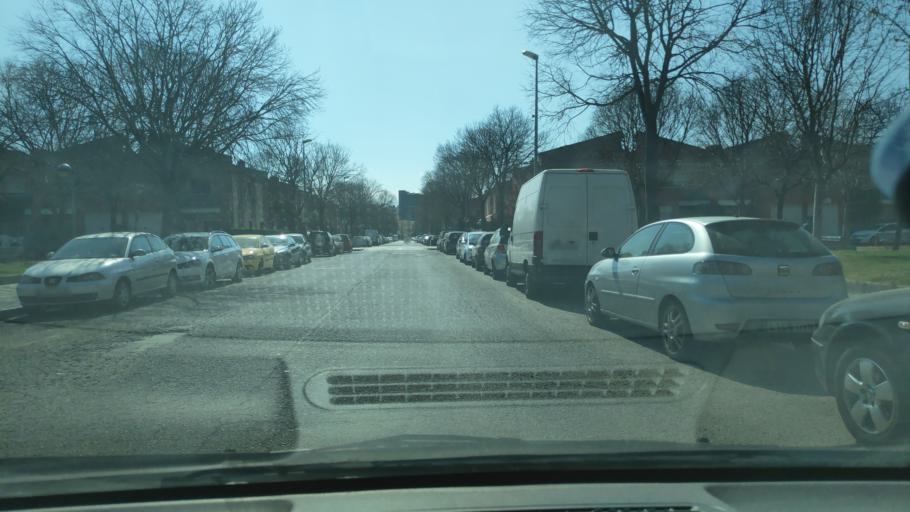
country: ES
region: Catalonia
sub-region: Provincia de Barcelona
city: Mollet del Valles
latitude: 41.5399
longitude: 2.2201
